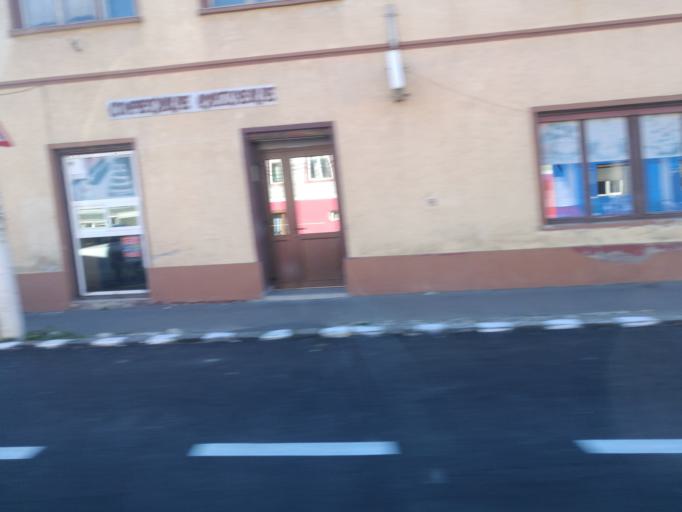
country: RO
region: Brasov
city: Codlea
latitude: 45.6966
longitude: 25.4457
